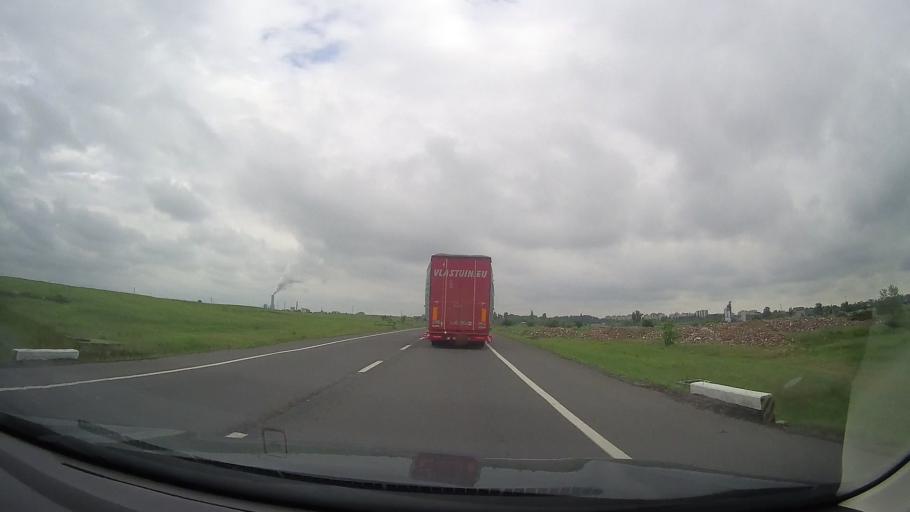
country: RO
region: Dolj
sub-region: Municipiul Craiova
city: Cernele
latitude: 44.3556
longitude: 23.7709
